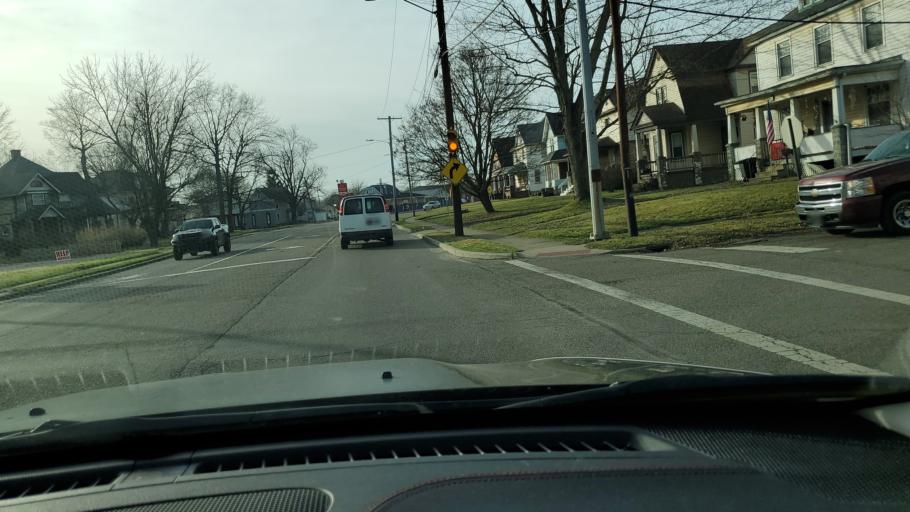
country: US
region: Ohio
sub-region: Trumbull County
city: Niles
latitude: 41.1883
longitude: -80.7658
